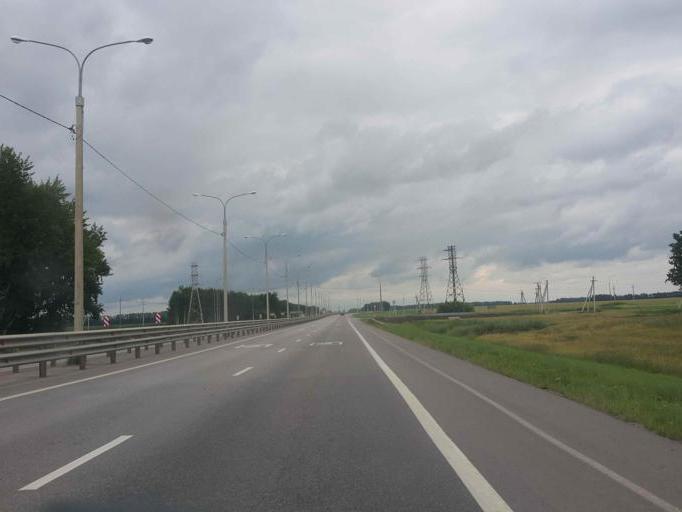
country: RU
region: Tambov
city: Zavoronezhskoye
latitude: 52.8486
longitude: 40.8078
